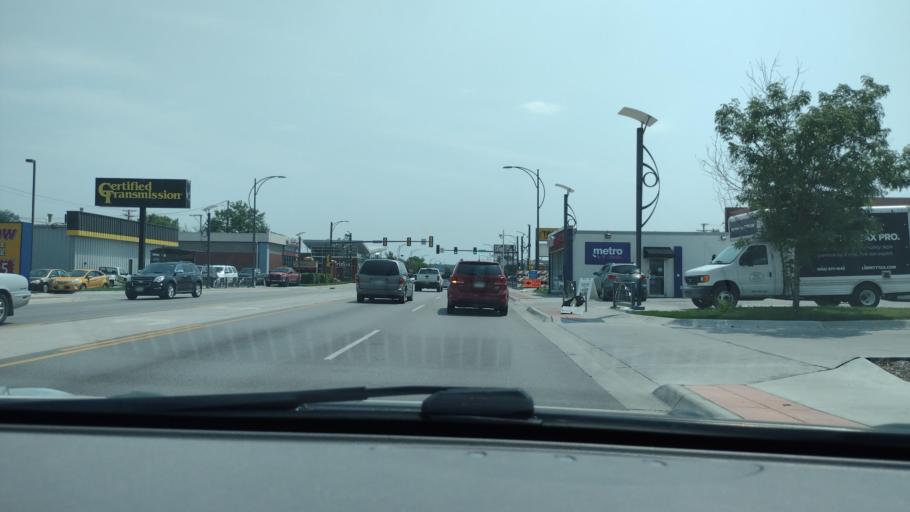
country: US
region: Iowa
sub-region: Pottawattamie County
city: Council Bluffs
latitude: 41.2619
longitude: -95.8767
